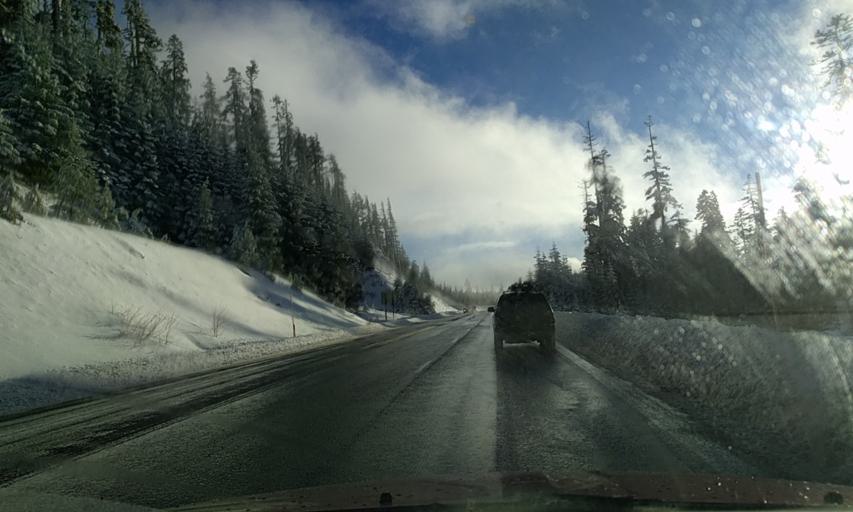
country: US
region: Oregon
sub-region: Clackamas County
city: Mount Hood Village
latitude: 45.2888
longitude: -121.6866
